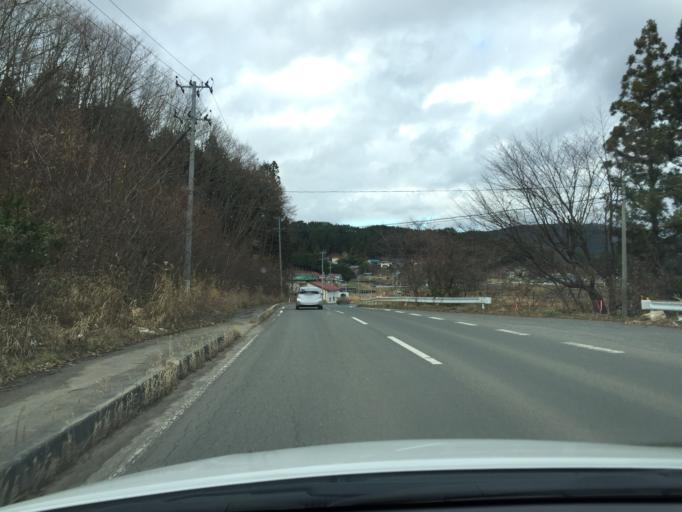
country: JP
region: Fukushima
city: Yanagawamachi-saiwaicho
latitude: 37.7117
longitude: 140.6940
